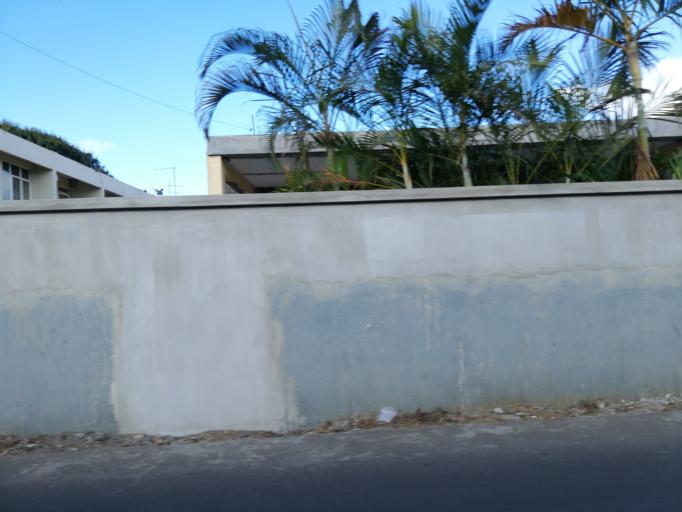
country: MU
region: Moka
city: Moka
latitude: -20.2231
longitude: 57.4754
